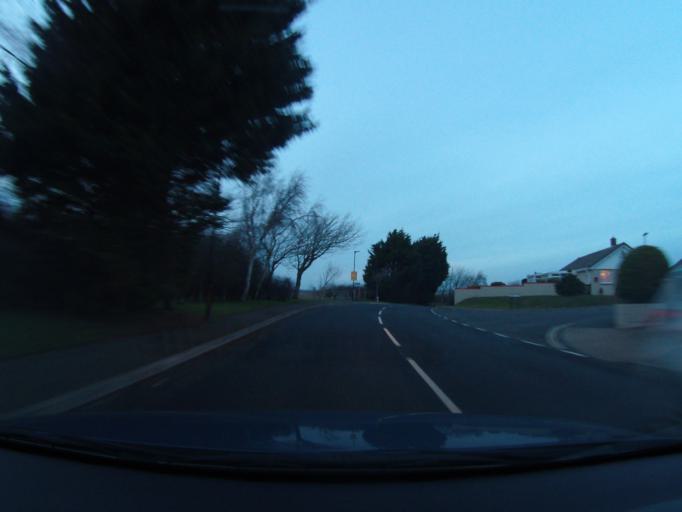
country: GB
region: England
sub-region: Isle of Wight
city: Shanklin
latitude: 50.6433
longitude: -1.1804
